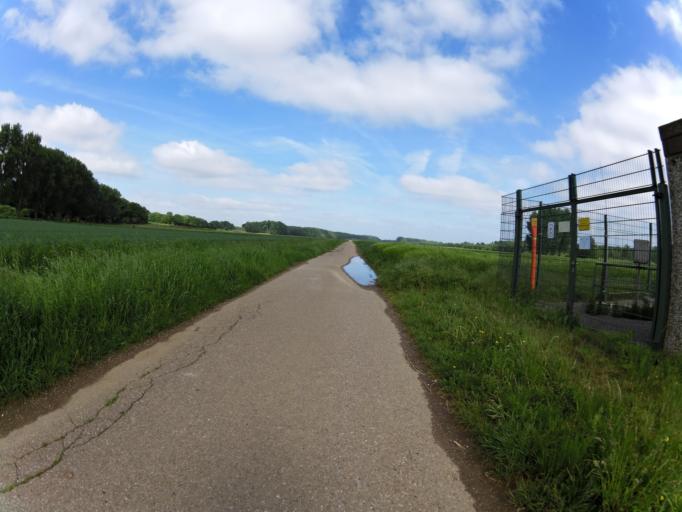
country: DE
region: North Rhine-Westphalia
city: Huckelhoven
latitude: 51.0158
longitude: 6.2204
